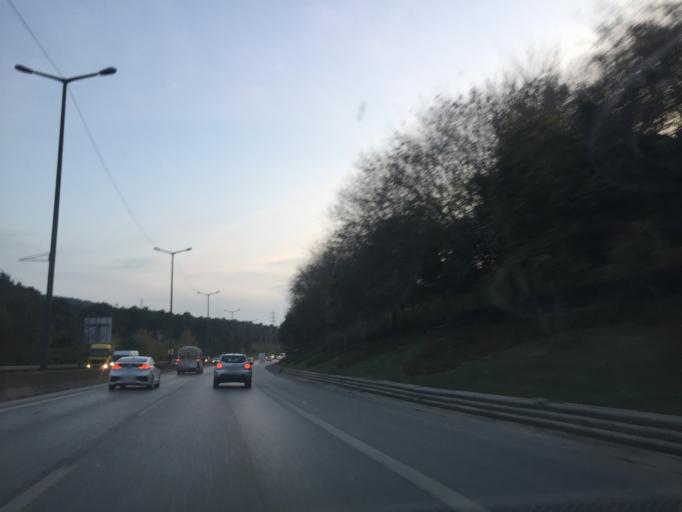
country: TR
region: Istanbul
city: Samandira
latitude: 40.9552
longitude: 29.2220
